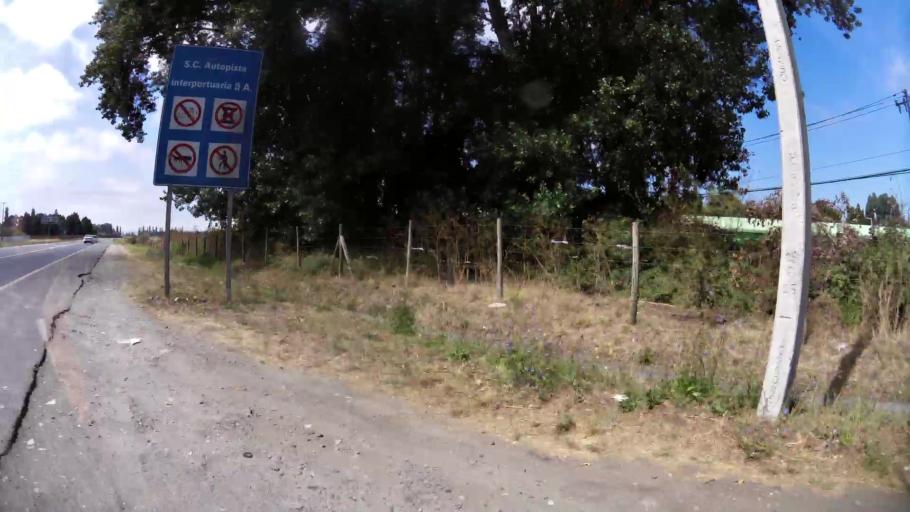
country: CL
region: Biobio
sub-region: Provincia de Concepcion
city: Concepcion
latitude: -36.7776
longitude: -73.0564
